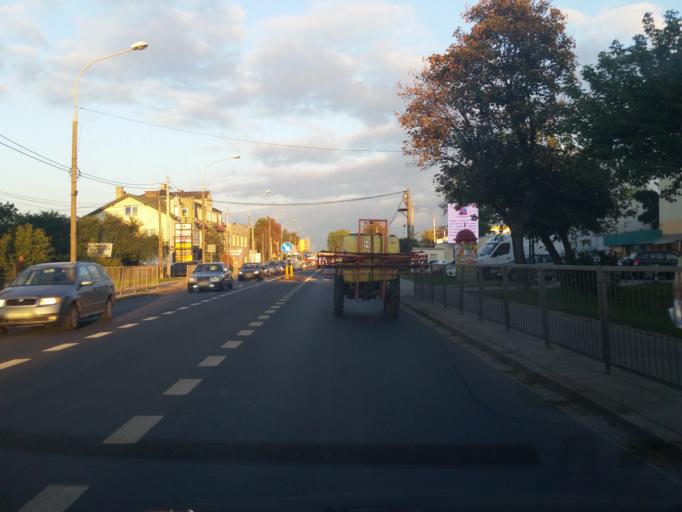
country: PL
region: Masovian Voivodeship
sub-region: Powiat warszawski zachodni
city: Ozarow Mazowiecki
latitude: 52.2101
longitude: 20.8033
